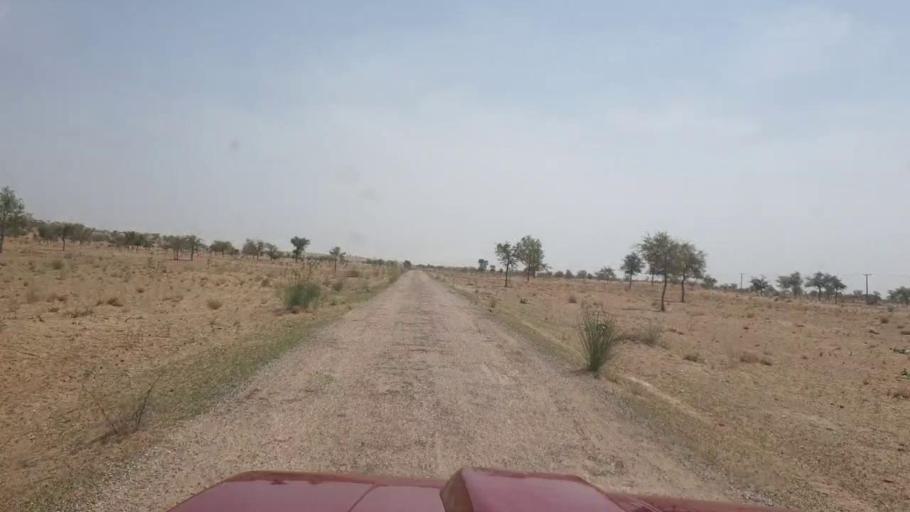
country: PK
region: Sindh
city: Islamkot
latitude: 25.1344
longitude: 70.3887
